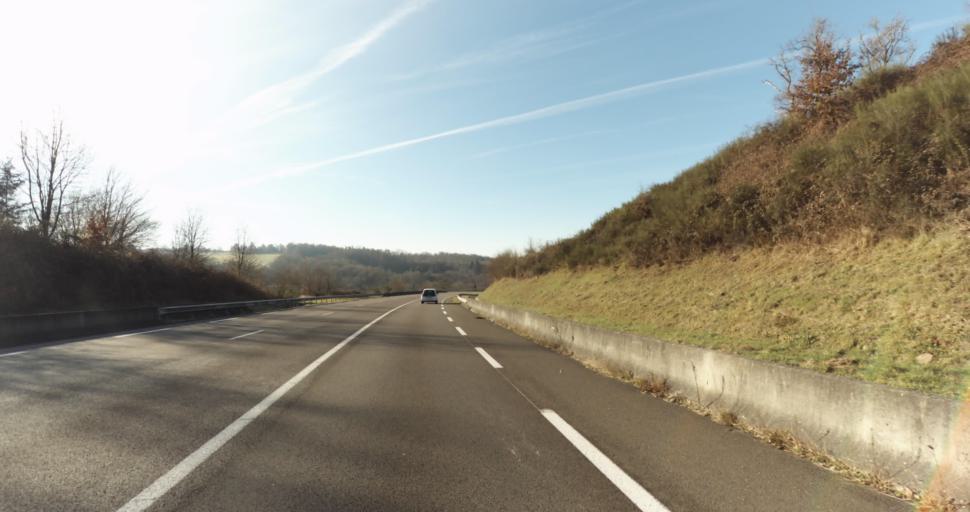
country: FR
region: Limousin
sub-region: Departement de la Haute-Vienne
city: Aixe-sur-Vienne
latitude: 45.8297
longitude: 1.1456
